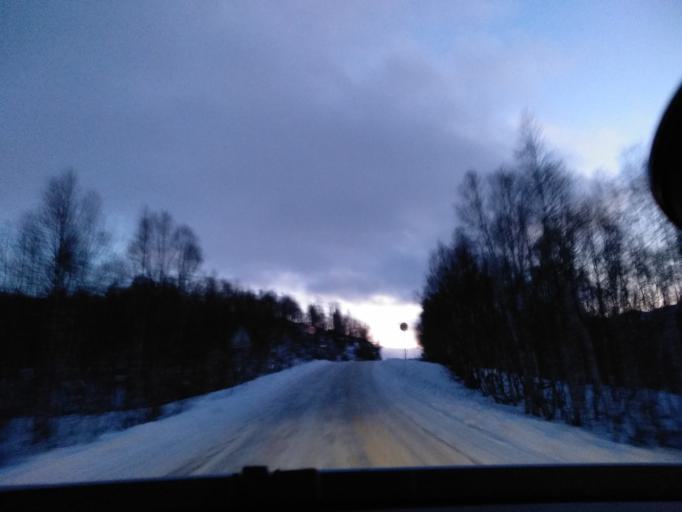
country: NO
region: Vest-Agder
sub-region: Sirdal
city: Tonstad
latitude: 59.0180
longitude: 6.9380
